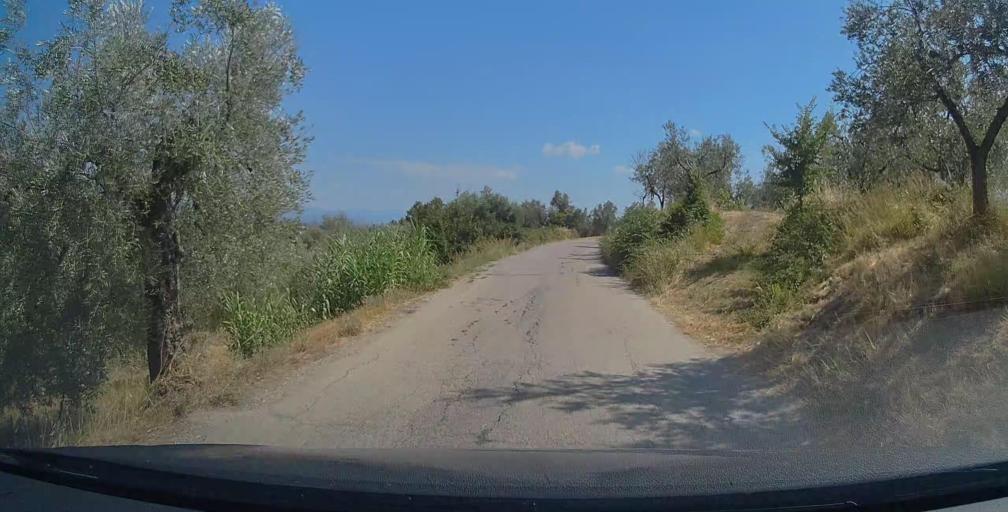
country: IT
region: Umbria
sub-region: Provincia di Terni
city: Calvi dell'Umbria
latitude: 42.3845
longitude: 12.5687
